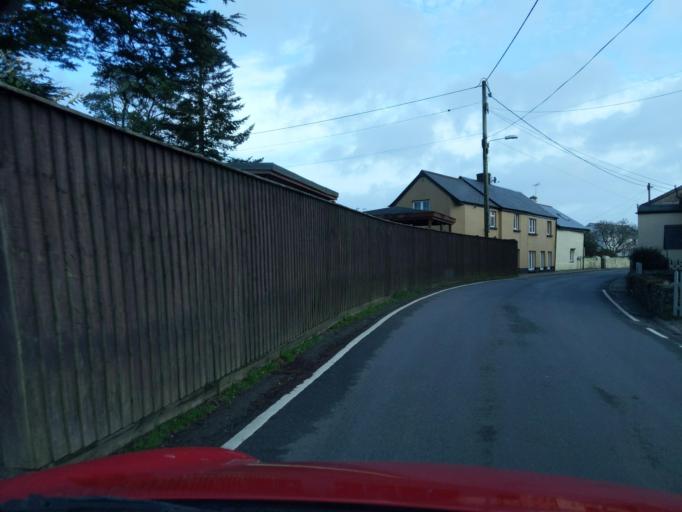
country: GB
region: England
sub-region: Devon
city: Great Torrington
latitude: 50.9196
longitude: -4.2085
